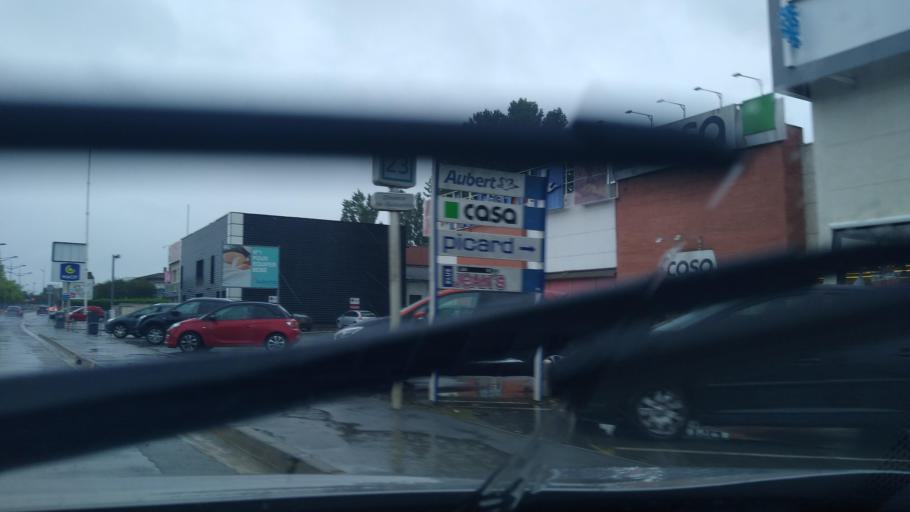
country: FR
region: Midi-Pyrenees
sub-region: Departement de la Haute-Garonne
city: Balma
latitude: 43.6317
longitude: 1.4820
